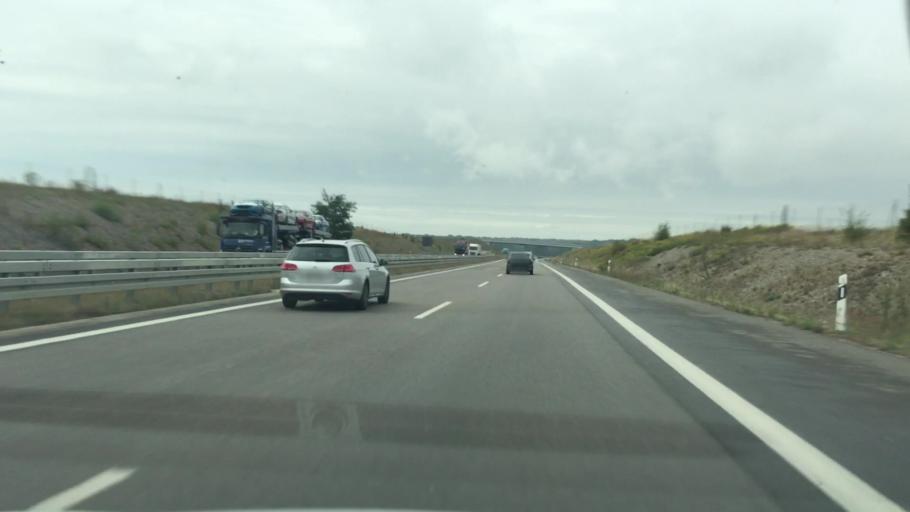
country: DE
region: Saxony
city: Narsdorf
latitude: 51.0031
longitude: 12.6881
